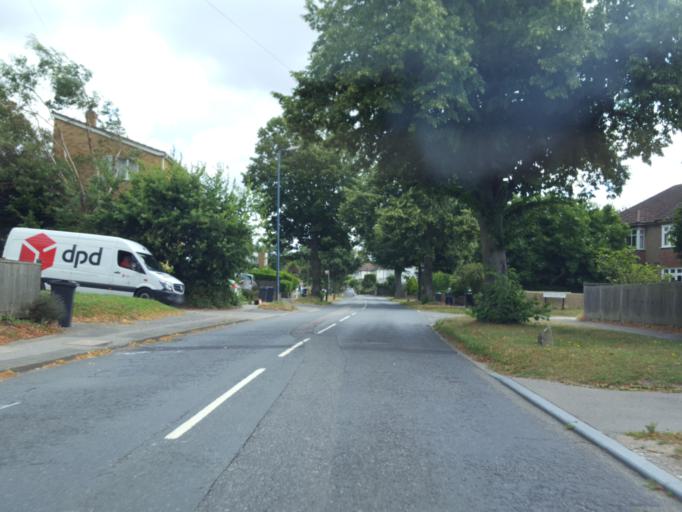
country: GB
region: England
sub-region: Kent
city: Boxley
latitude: 51.2892
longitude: 0.5318
